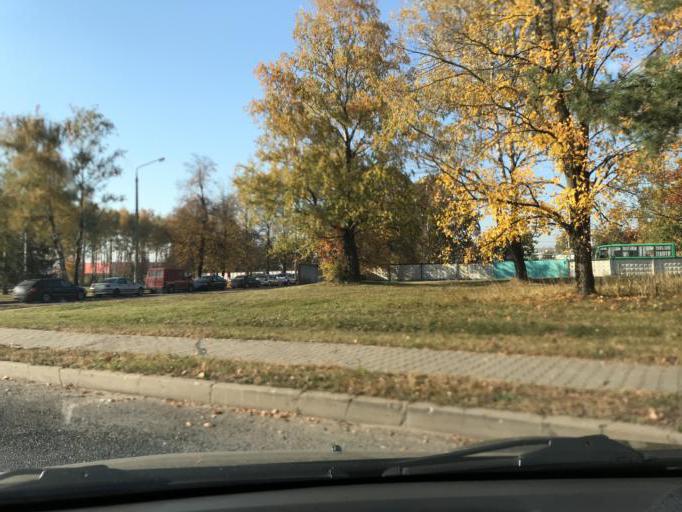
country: BY
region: Minsk
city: Pryvol'ny
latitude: 53.8070
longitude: 27.7935
